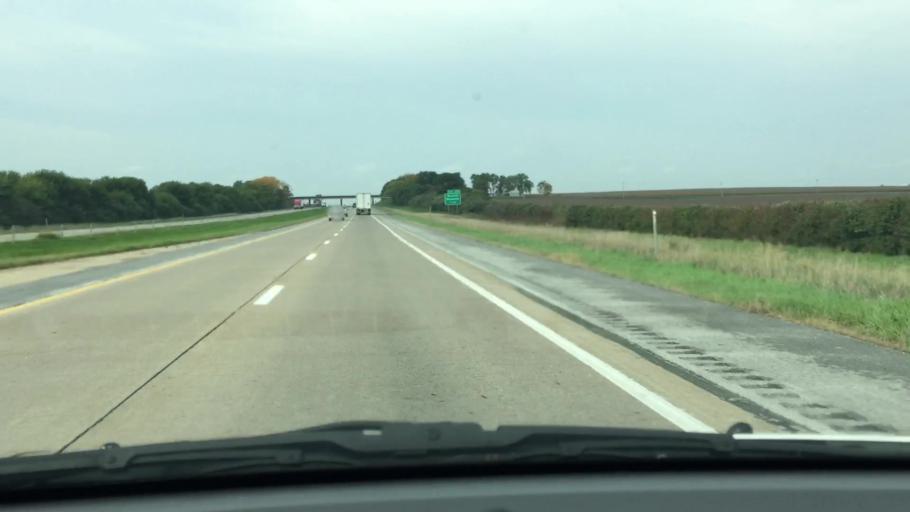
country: US
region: Iowa
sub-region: Cedar County
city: Durant
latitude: 41.6331
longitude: -90.8927
